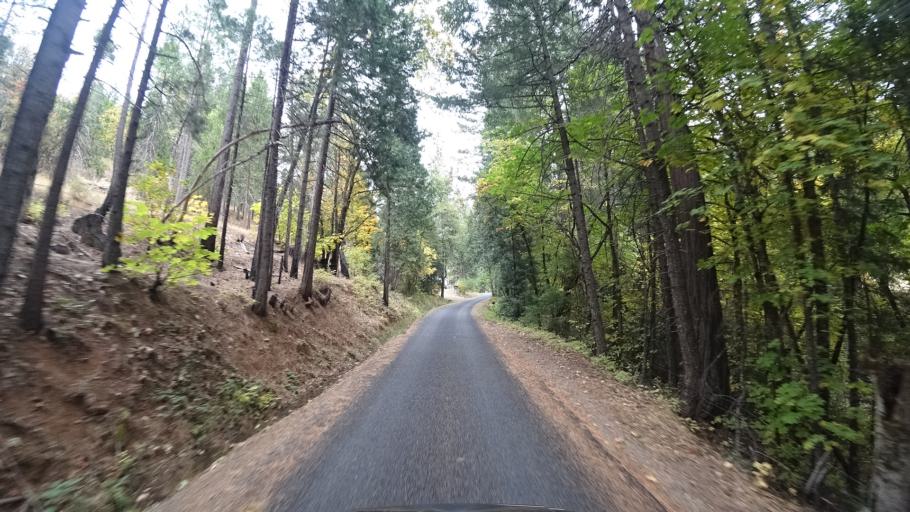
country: US
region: California
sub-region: Siskiyou County
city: Happy Camp
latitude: 41.8690
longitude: -123.1390
